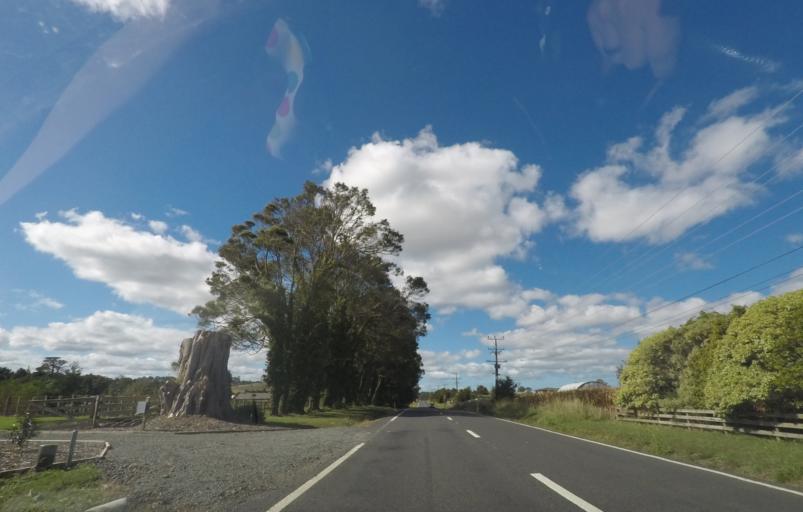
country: NZ
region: Auckland
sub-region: Auckland
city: Parakai
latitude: -36.6146
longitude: 174.5764
